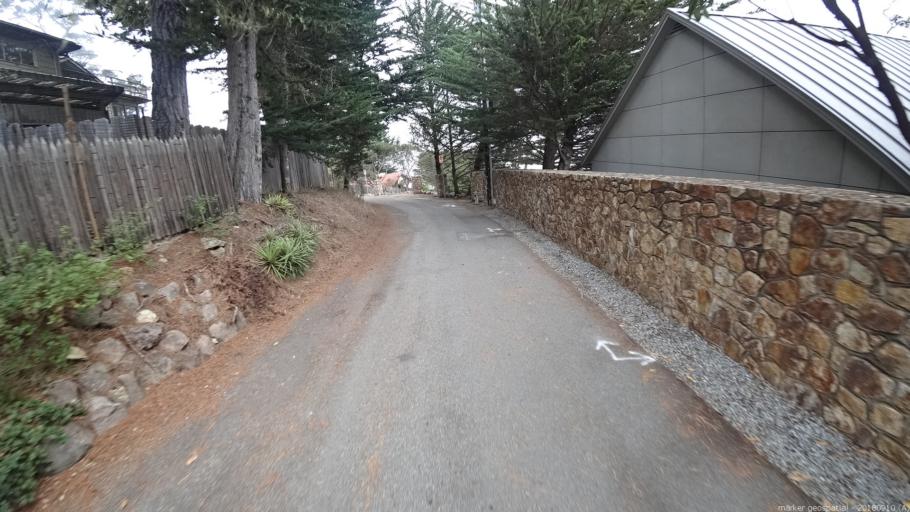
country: US
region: California
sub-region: Monterey County
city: Carmel-by-the-Sea
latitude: 36.4924
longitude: -121.9393
